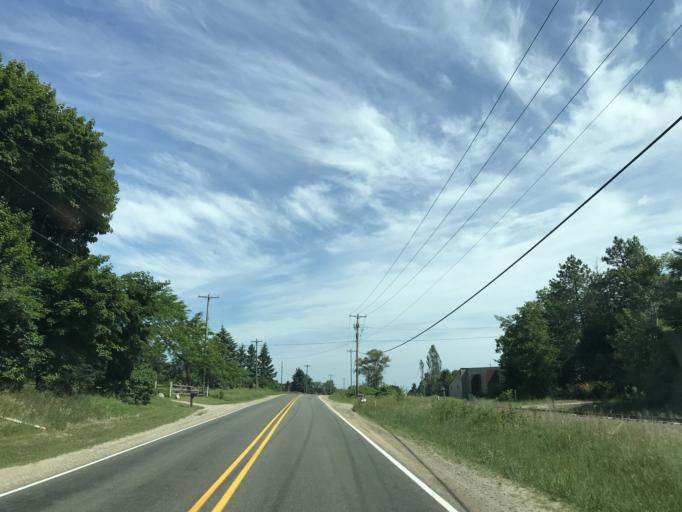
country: US
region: Michigan
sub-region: Grand Traverse County
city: Traverse City
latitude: 44.7112
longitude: -85.6267
